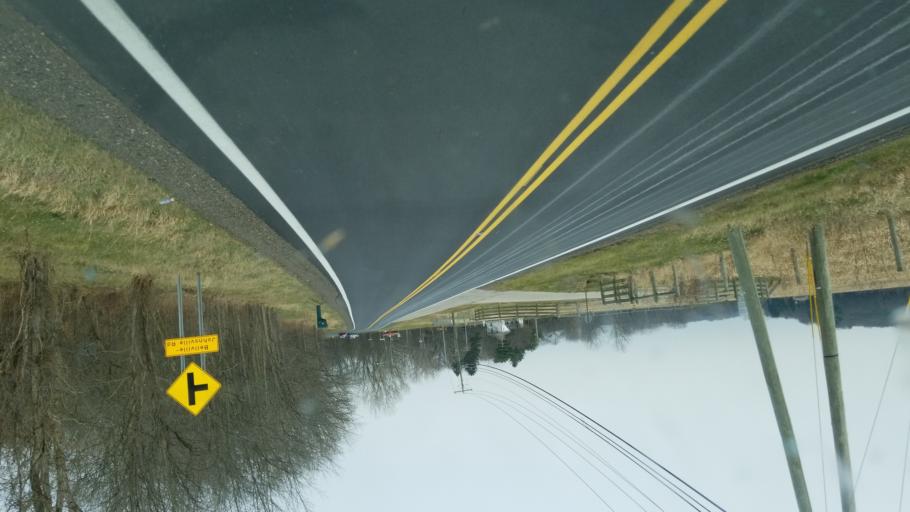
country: US
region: Ohio
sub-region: Sandusky County
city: Bellville
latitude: 40.6219
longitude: -82.5262
